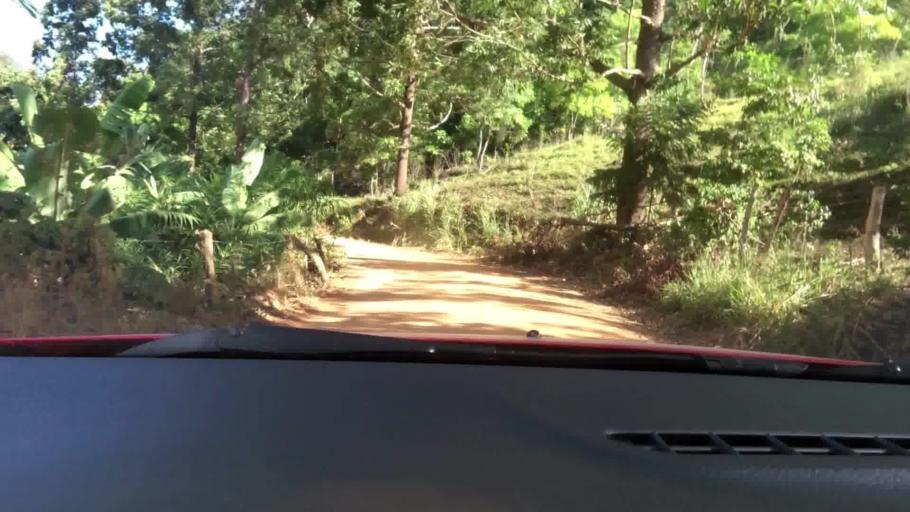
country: BR
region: Espirito Santo
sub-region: Guarapari
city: Guarapari
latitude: -20.5245
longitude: -40.5664
